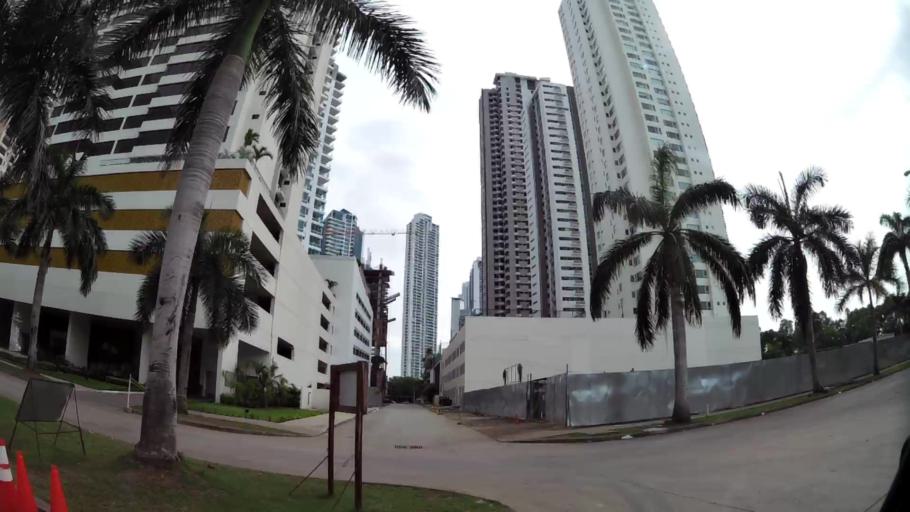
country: PA
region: Panama
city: San Miguelito
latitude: 9.0100
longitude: -79.4725
